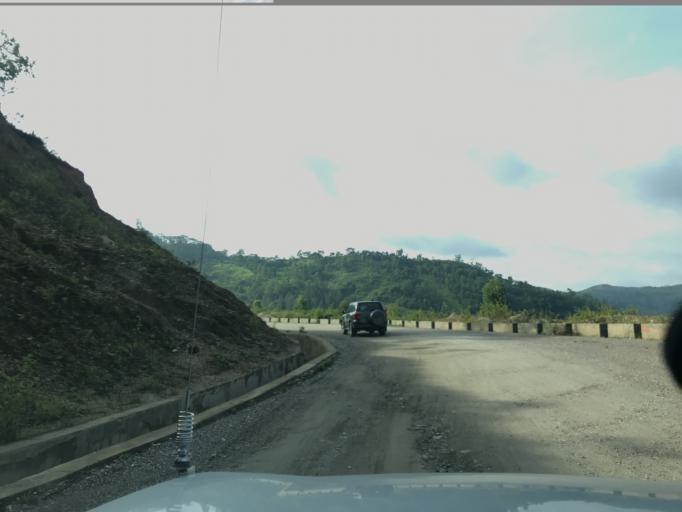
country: TL
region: Aileu
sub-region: Aileu Villa
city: Aileu
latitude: -8.6631
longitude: 125.5455
